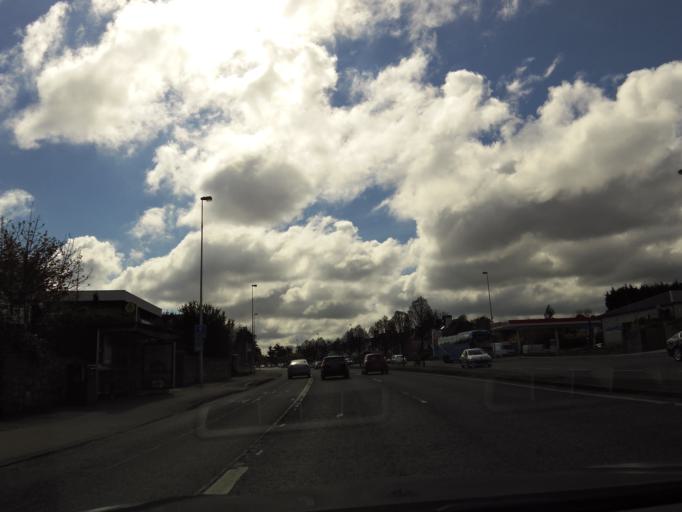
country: IE
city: Booterstown
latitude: 53.2964
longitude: -6.2034
